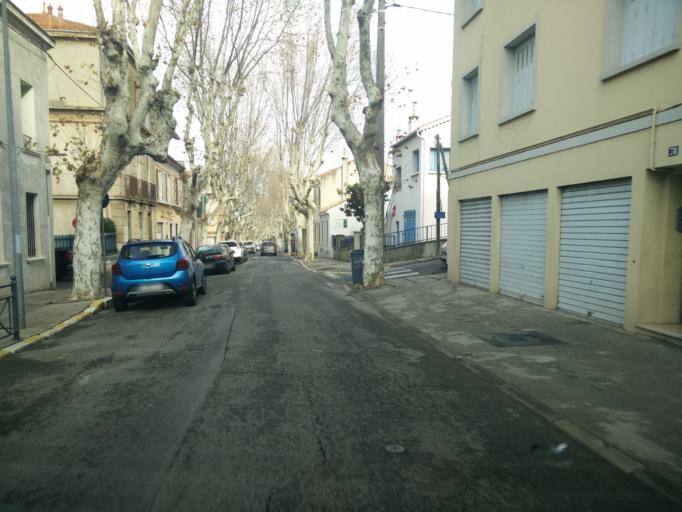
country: FR
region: Provence-Alpes-Cote d'Azur
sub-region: Departement du Var
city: La Seyne-sur-Mer
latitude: 43.0947
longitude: 5.8837
